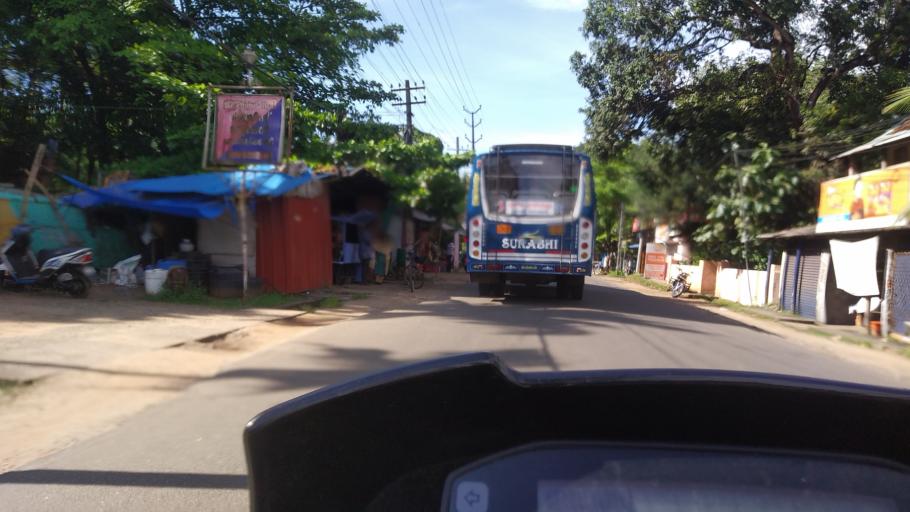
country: IN
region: Kerala
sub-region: Ernakulam
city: Elur
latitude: 10.0392
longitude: 76.2194
